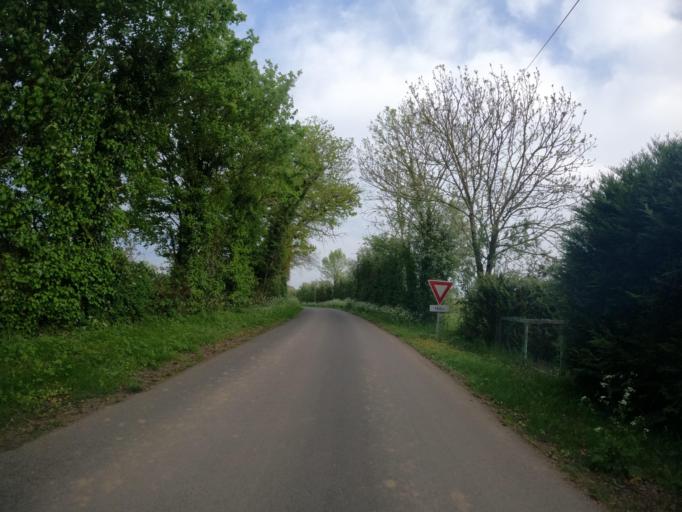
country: FR
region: Poitou-Charentes
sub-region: Departement des Deux-Sevres
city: La Chapelle-Saint-Laurent
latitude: 46.6981
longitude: -0.4902
